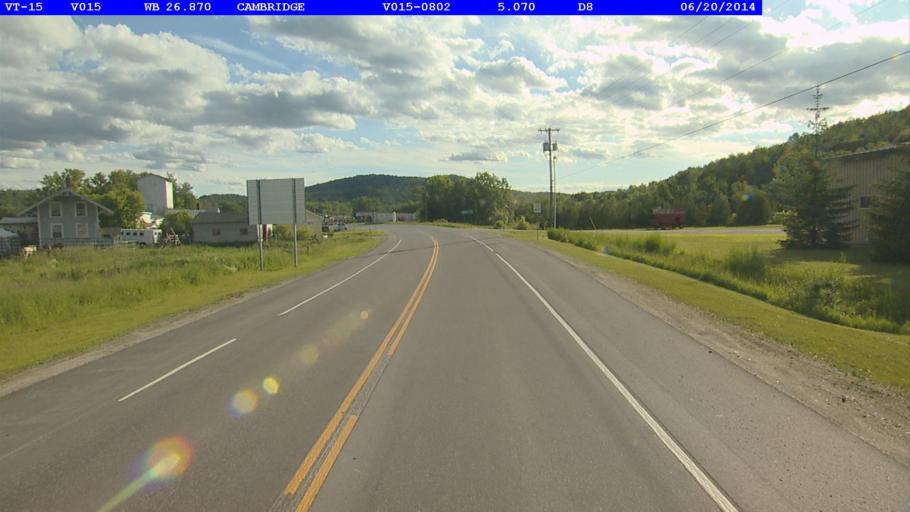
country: US
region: Vermont
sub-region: Lamoille County
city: Johnson
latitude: 44.6473
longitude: -72.8307
